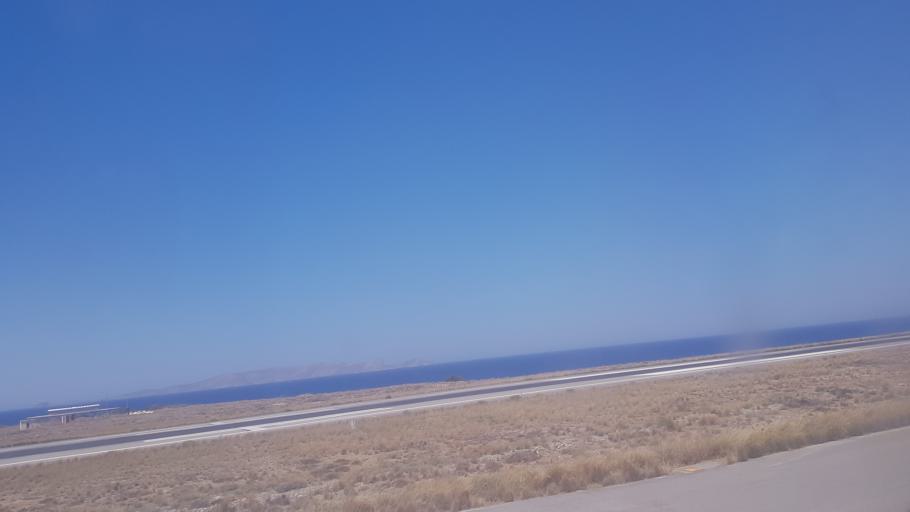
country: GR
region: Crete
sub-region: Nomos Irakleiou
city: Nea Alikarnassos
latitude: 35.3385
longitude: 25.1848
